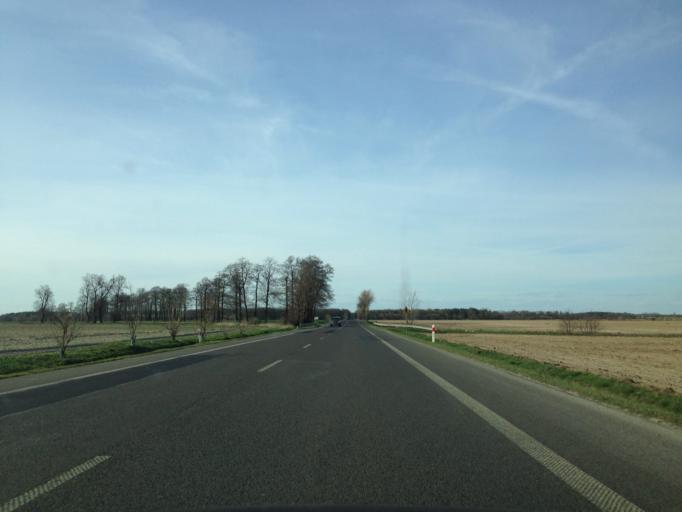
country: PL
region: Lodz Voivodeship
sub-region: Powiat kutnowski
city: Ostrowy
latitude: 52.3347
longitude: 19.1493
